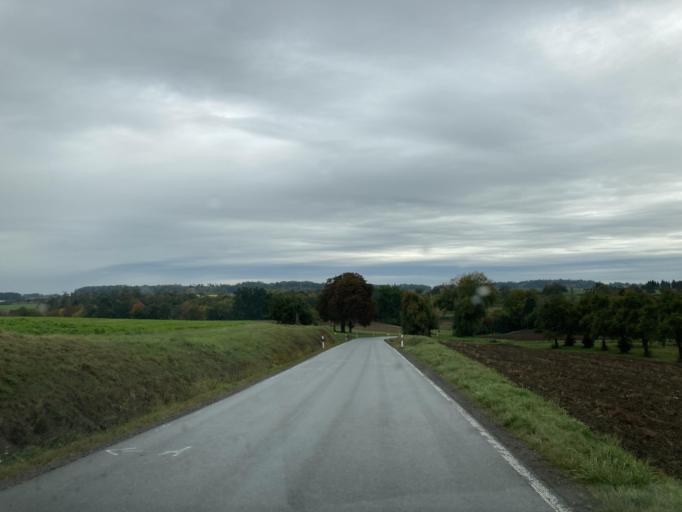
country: DE
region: Baden-Wuerttemberg
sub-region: Regierungsbezirk Stuttgart
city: Bondorf
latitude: 48.5383
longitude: 8.8770
